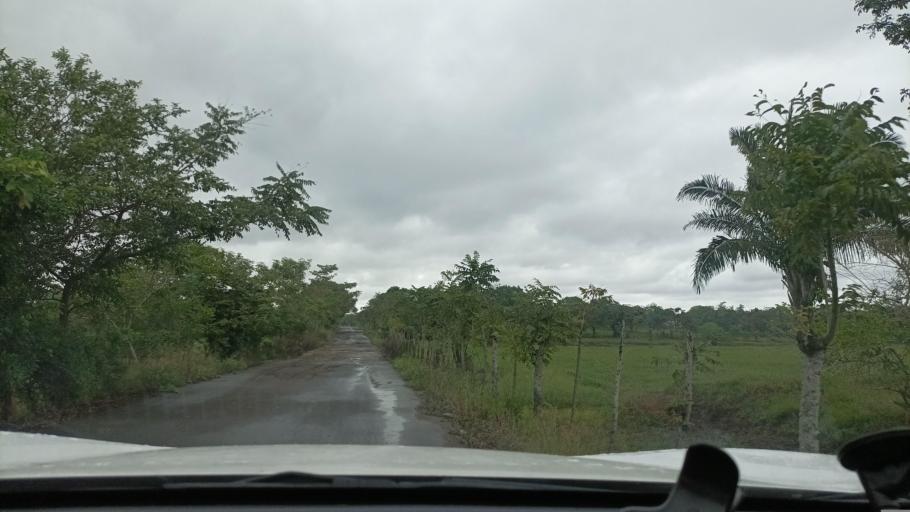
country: MX
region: Veracruz
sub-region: Moloacan
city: Cuichapa
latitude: 17.7694
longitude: -94.3884
